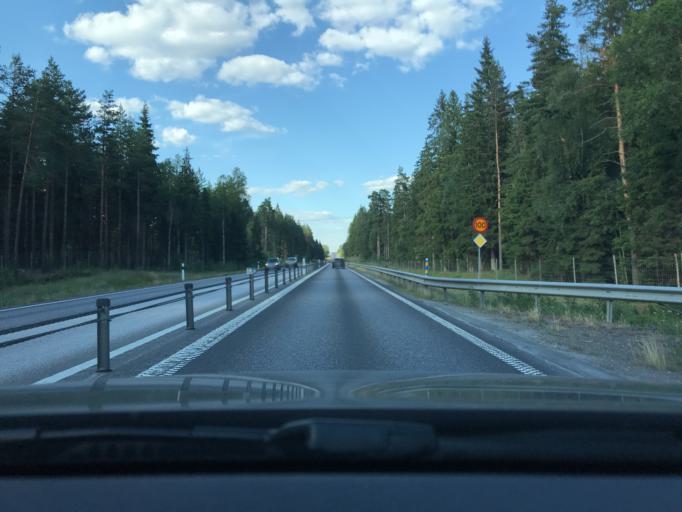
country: SE
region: Kronoberg
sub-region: Vaxjo Kommun
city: Rottne
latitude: 56.9466
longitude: 14.9188
